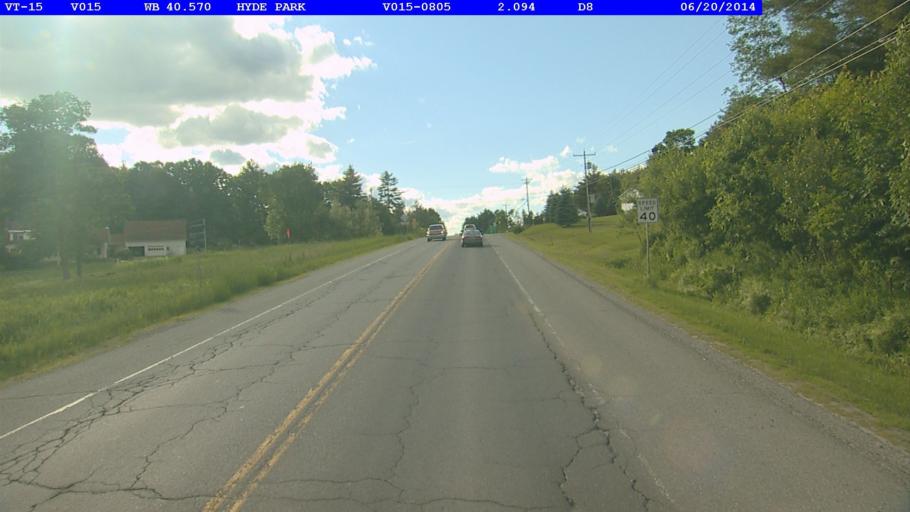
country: US
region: Vermont
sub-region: Lamoille County
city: Hyde Park
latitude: 44.5949
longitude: -72.6118
